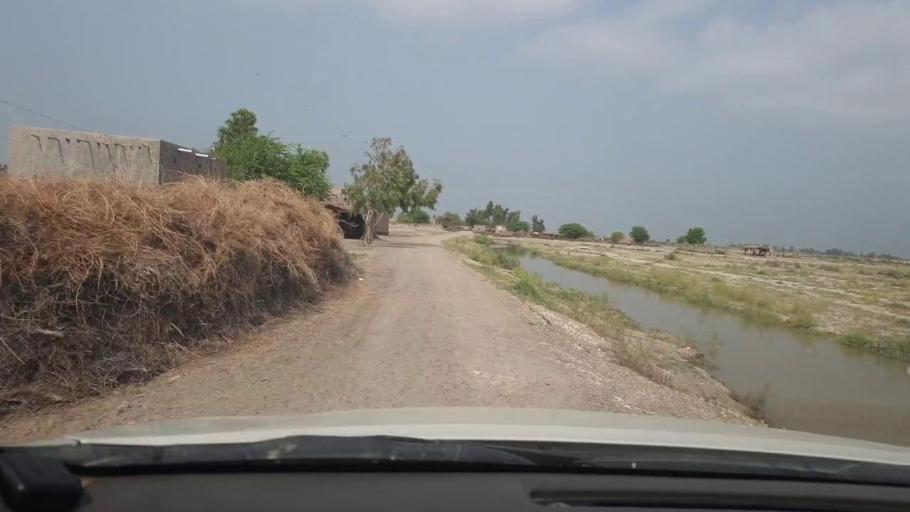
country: PK
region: Sindh
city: Shikarpur
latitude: 28.0252
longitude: 68.5868
